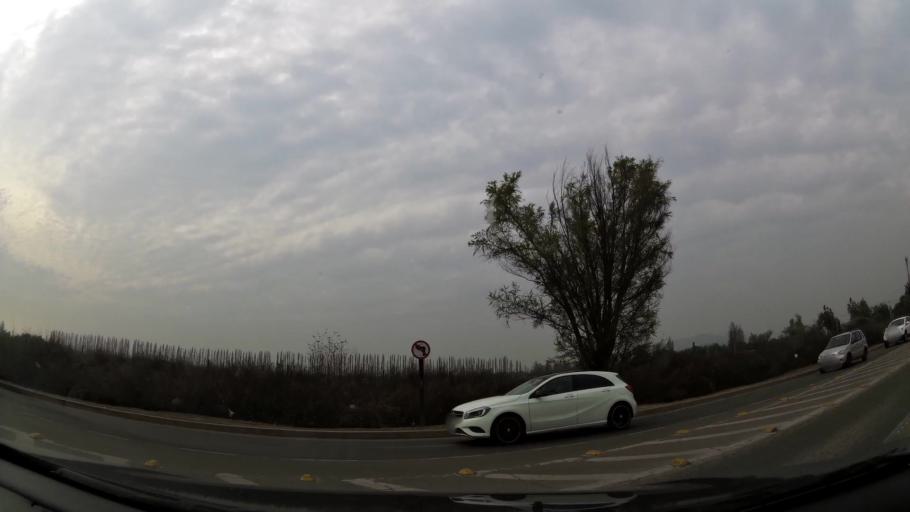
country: CL
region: Santiago Metropolitan
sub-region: Provincia de Chacabuco
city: Chicureo Abajo
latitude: -33.2856
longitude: -70.6978
